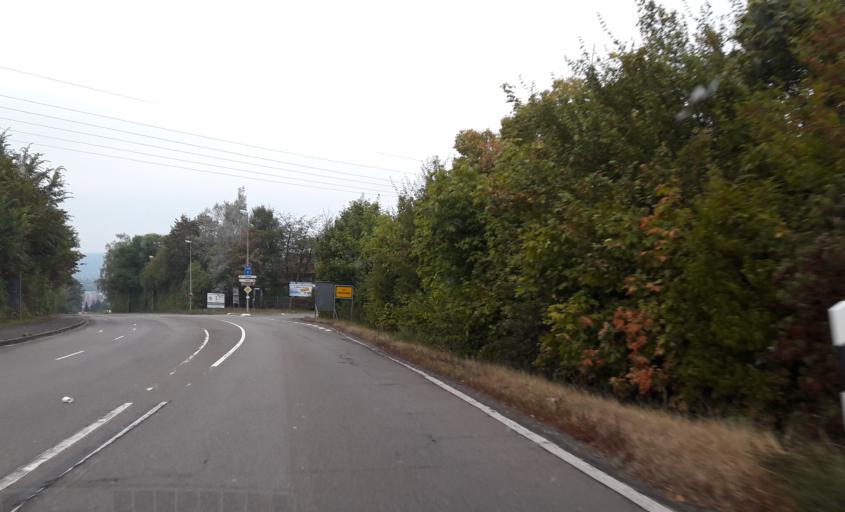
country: DE
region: Rheinland-Pfalz
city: Zweibrucken
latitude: 49.2425
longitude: 7.3887
